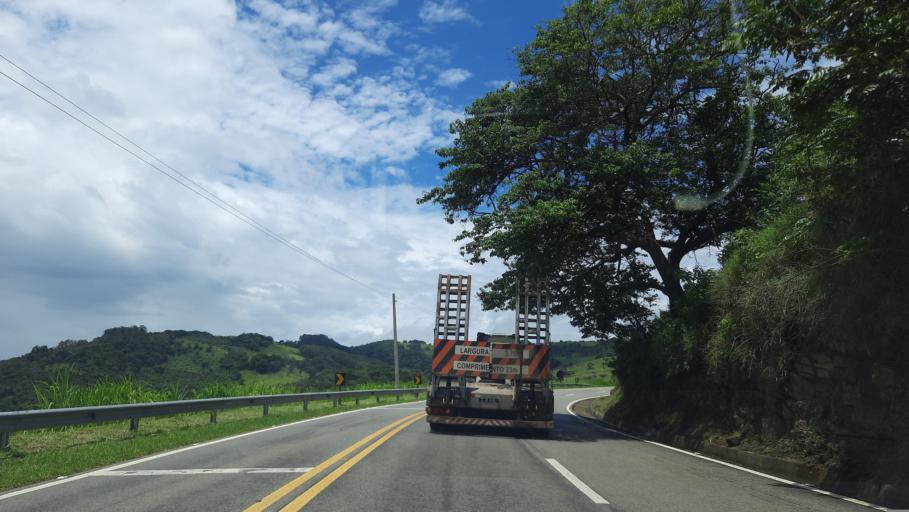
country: BR
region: Sao Paulo
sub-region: Vargem Grande Do Sul
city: Vargem Grande do Sul
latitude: -21.8314
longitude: -46.7647
